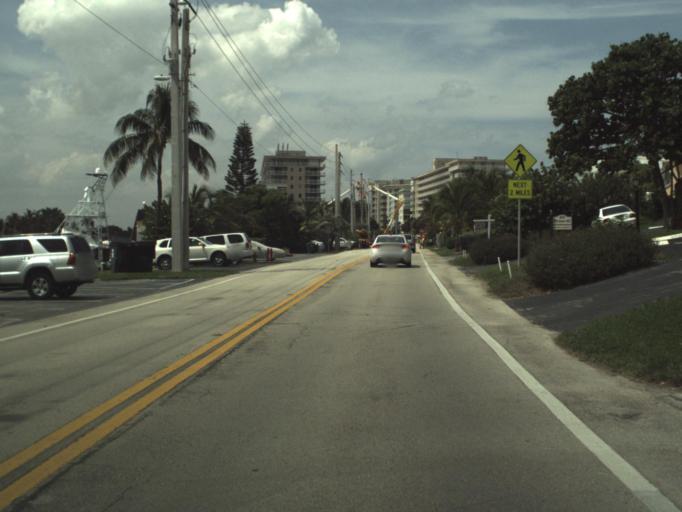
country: US
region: Florida
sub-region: Broward County
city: Lighthouse Point
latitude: 26.2766
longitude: -80.0802
